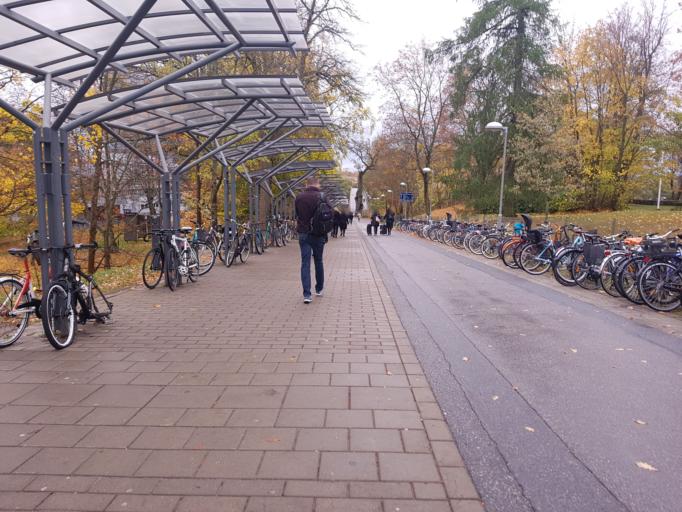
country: SE
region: Stockholm
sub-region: Stockholms Kommun
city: Arsta
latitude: 59.2781
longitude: 18.0115
